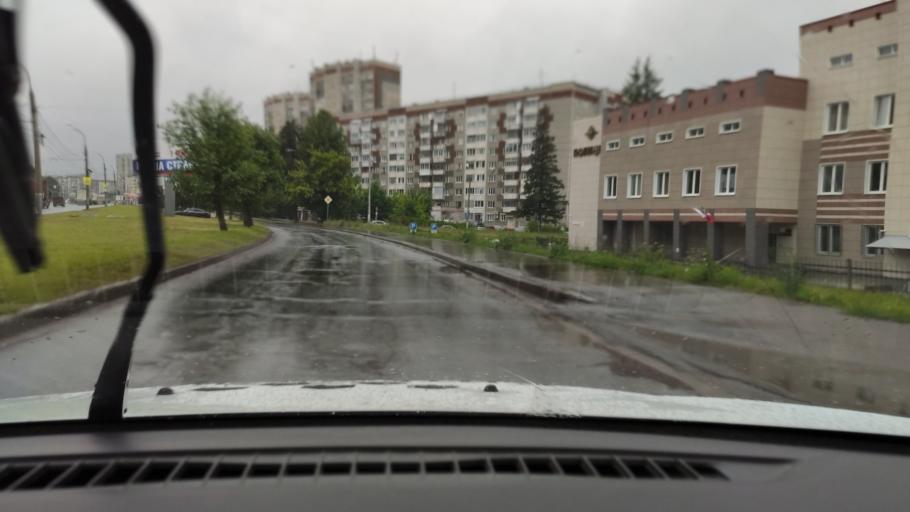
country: RU
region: Udmurtiya
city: Izhevsk
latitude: 56.8818
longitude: 53.2250
